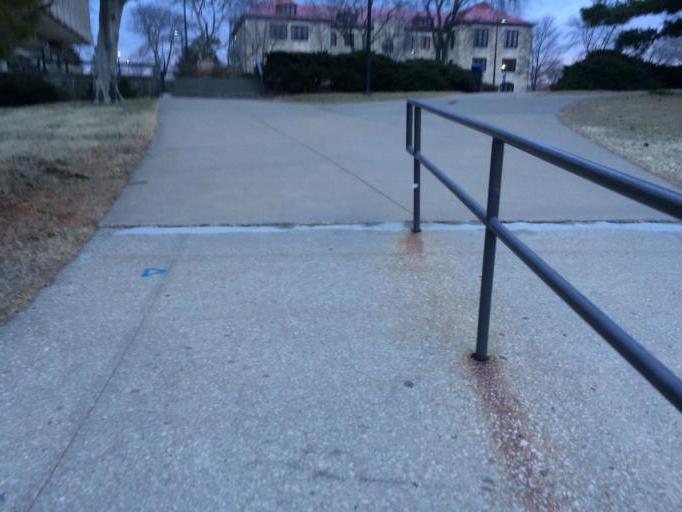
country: US
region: Kansas
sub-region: Douglas County
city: Lawrence
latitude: 38.9570
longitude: -95.2474
